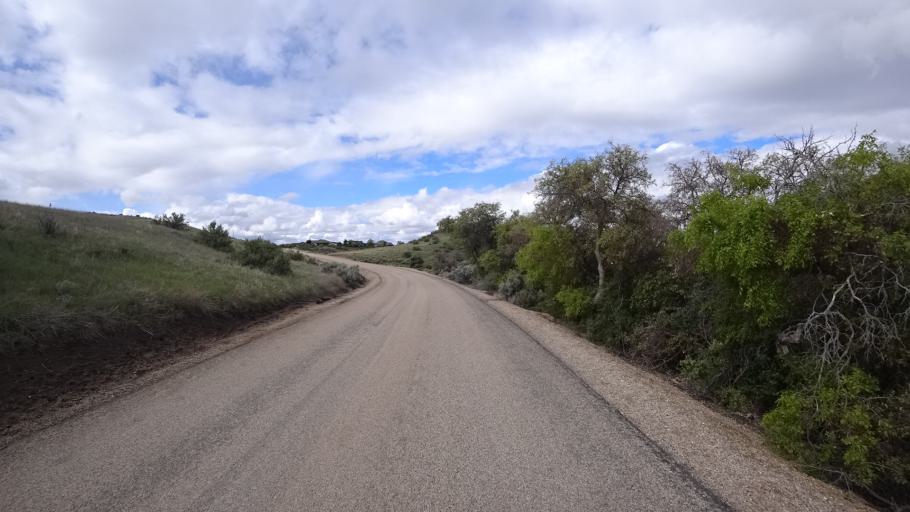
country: US
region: Idaho
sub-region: Ada County
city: Garden City
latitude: 43.7283
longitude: -116.2325
